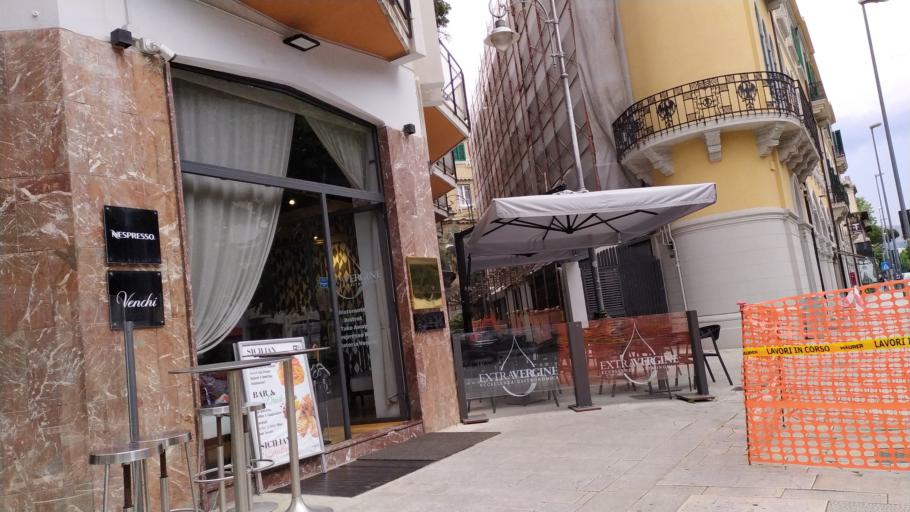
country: IT
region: Sicily
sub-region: Messina
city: Messina
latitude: 38.1903
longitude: 15.5564
